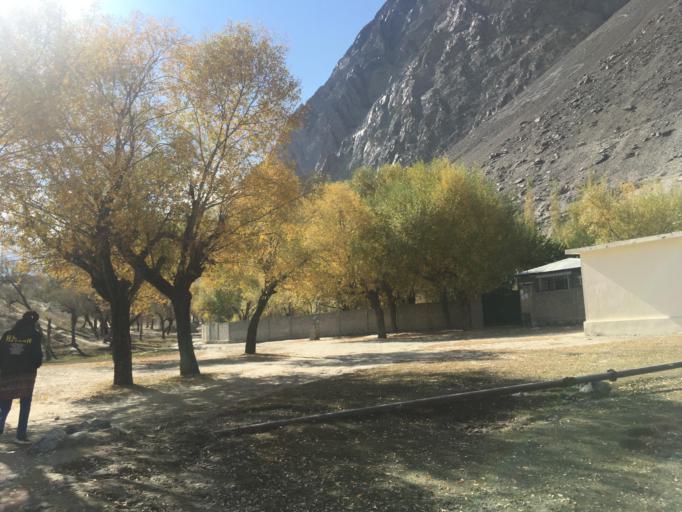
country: PK
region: Gilgit-Baltistan
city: Skardu
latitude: 35.3326
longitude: 75.5212
